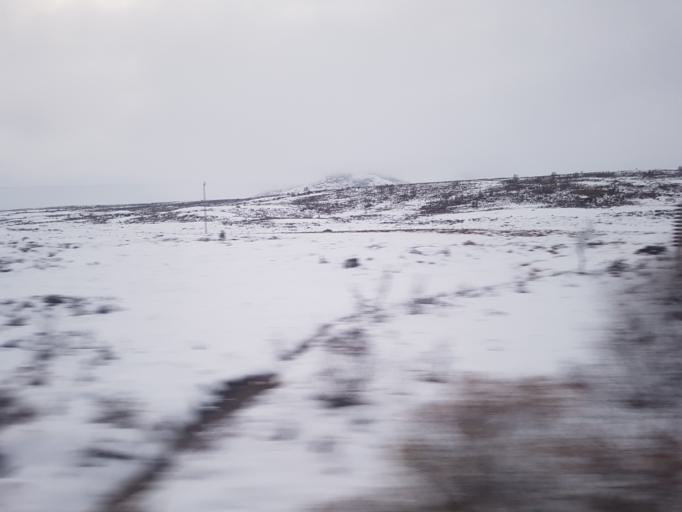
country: NO
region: Sor-Trondelag
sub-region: Oppdal
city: Oppdal
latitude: 62.2777
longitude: 9.5866
